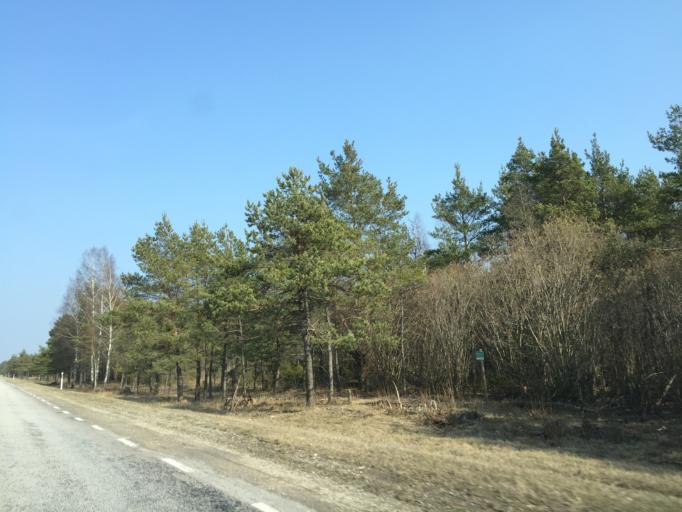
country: EE
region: Saare
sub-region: Kuressaare linn
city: Kuressaare
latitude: 58.3762
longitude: 22.7326
